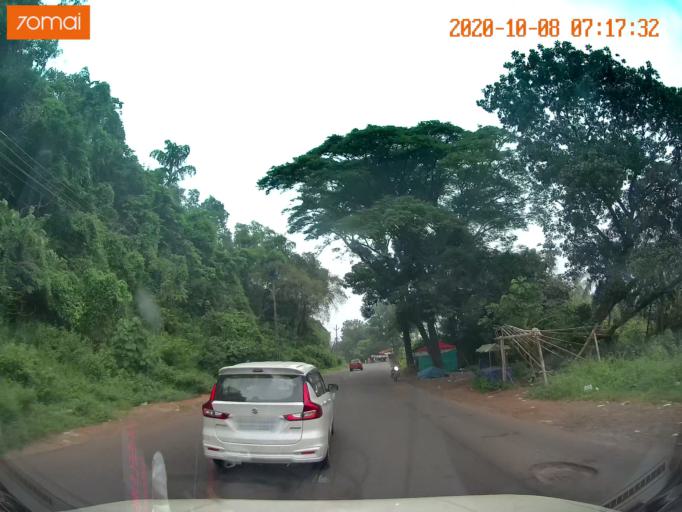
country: IN
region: Kerala
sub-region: Malappuram
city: Ponnani
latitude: 10.8373
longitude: 76.0194
